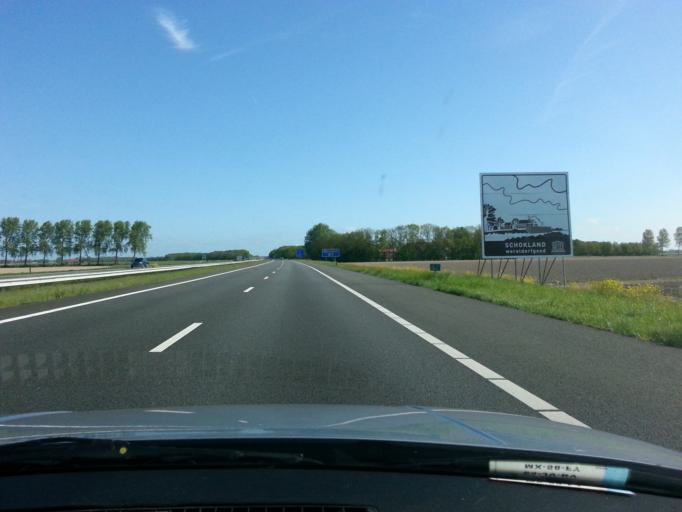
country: NL
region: Flevoland
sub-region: Gemeente Urk
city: Urk
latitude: 52.6305
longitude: 5.6684
